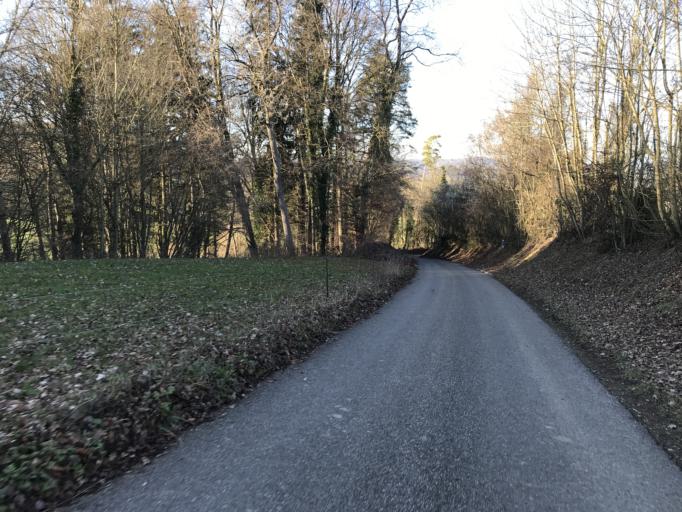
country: CH
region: Thurgau
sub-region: Frauenfeld District
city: Wagenhausen
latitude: 47.6444
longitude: 8.8502
